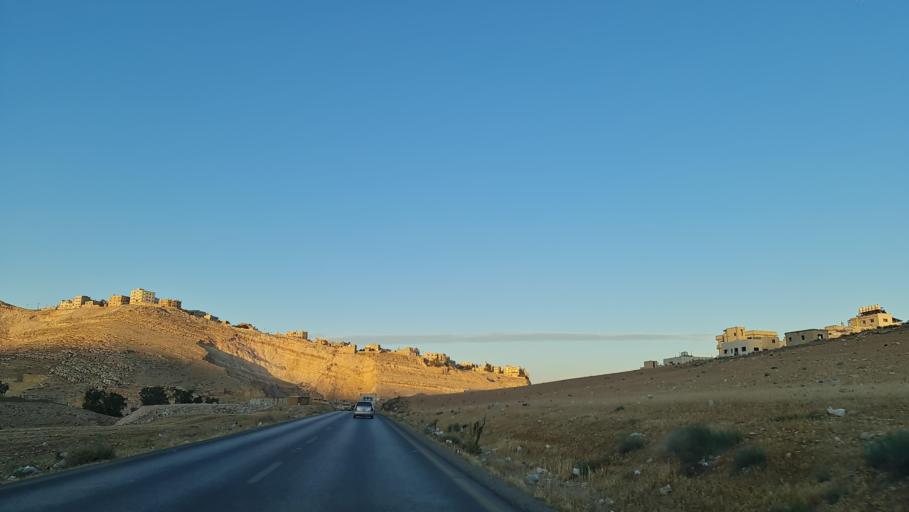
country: JO
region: Zarqa
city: Zarqa
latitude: 32.0821
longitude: 36.0626
